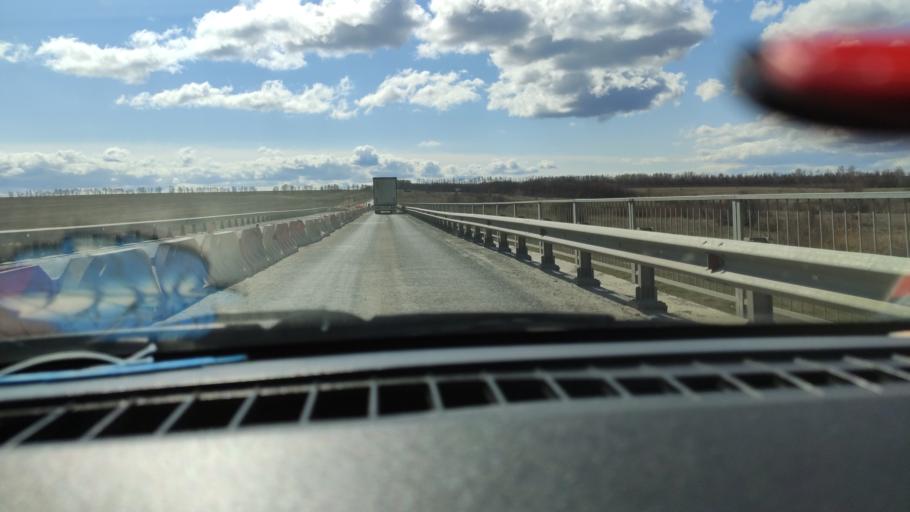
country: RU
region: Saratov
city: Dukhovnitskoye
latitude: 52.7341
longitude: 48.2573
